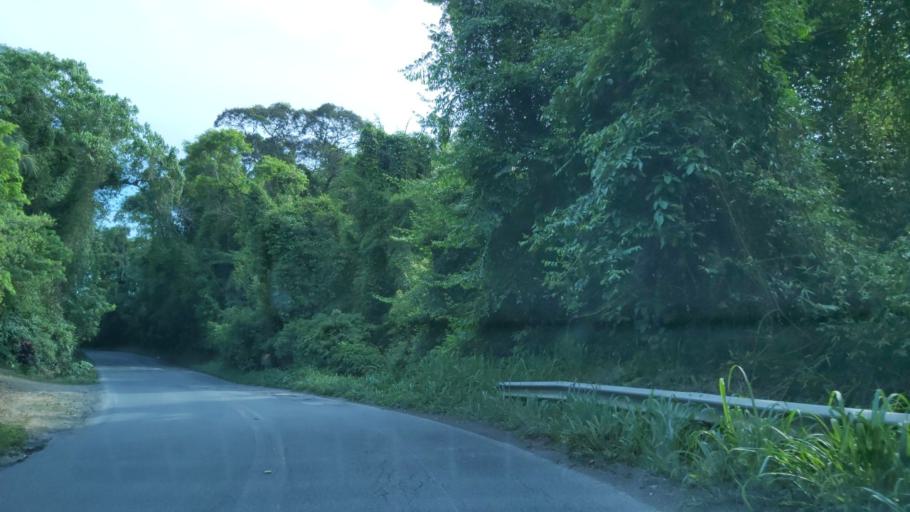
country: BR
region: Sao Paulo
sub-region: Juquia
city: Juquia
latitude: -24.0843
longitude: -47.6083
